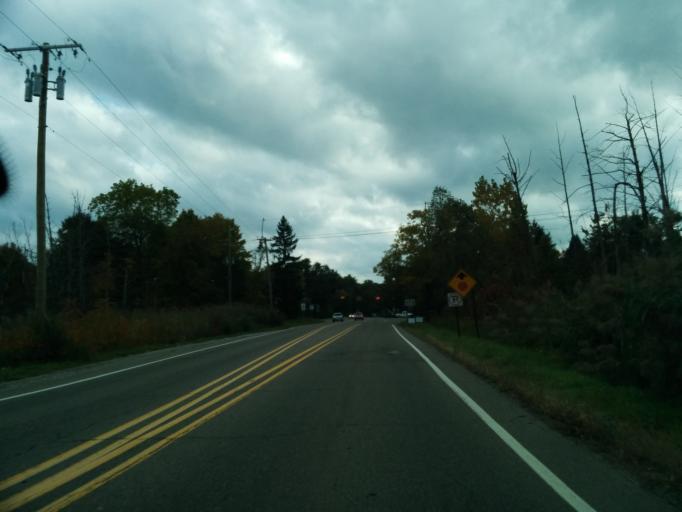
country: US
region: Michigan
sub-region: Oakland County
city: Waterford
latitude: 42.6696
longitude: -83.4891
